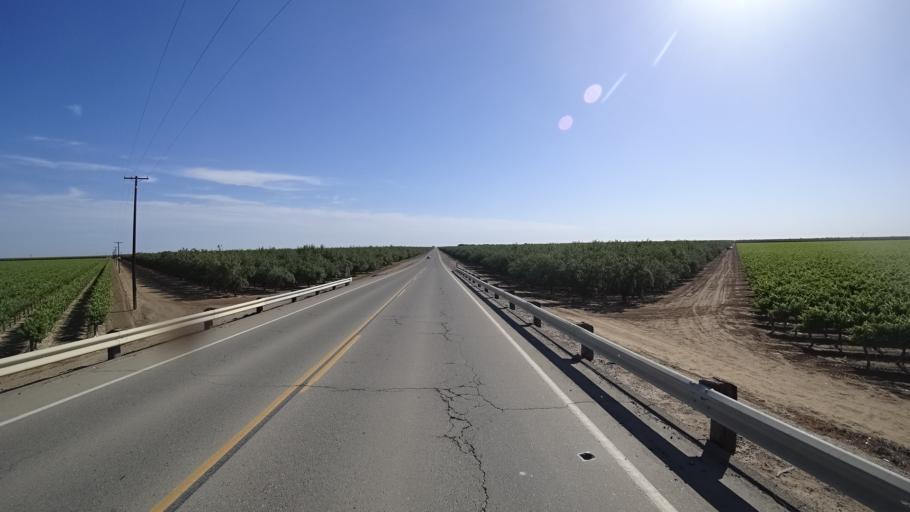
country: US
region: California
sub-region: Fresno County
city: Huron
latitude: 36.1015
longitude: -120.0576
